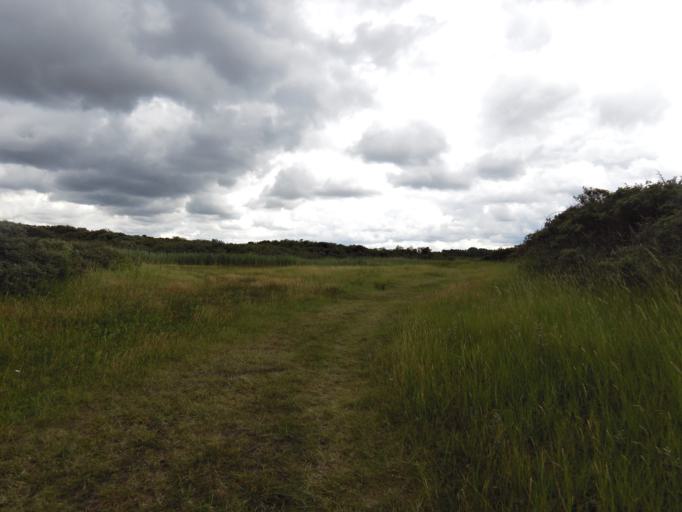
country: NL
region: South Holland
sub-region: Gemeente Goeree-Overflakkee
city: Goedereede
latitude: 51.8414
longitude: 3.9921
